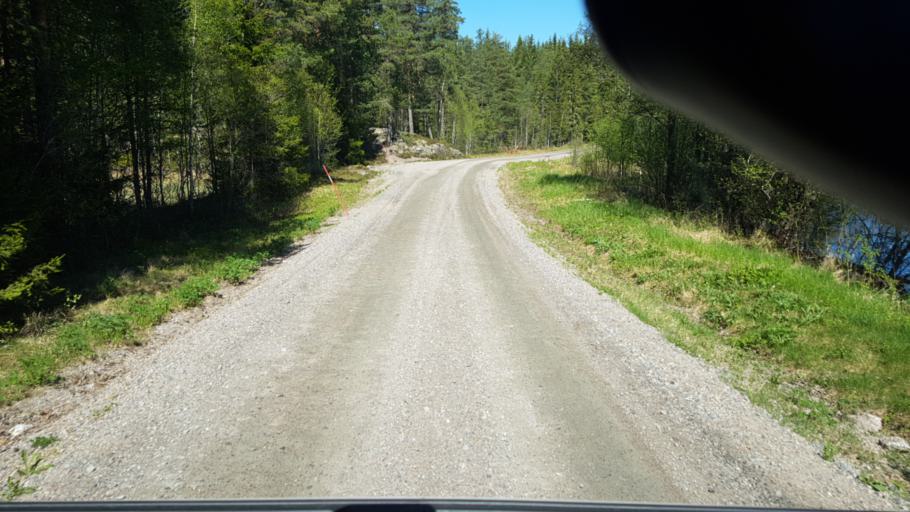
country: SE
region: Vaermland
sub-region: Eda Kommun
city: Charlottenberg
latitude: 60.0417
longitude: 12.5110
